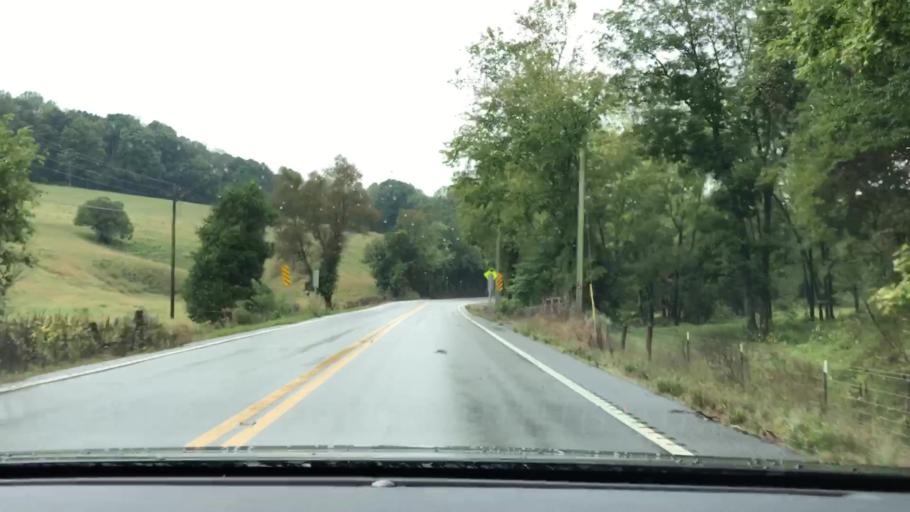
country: US
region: Tennessee
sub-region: Macon County
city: Red Boiling Springs
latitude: 36.5724
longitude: -85.7844
